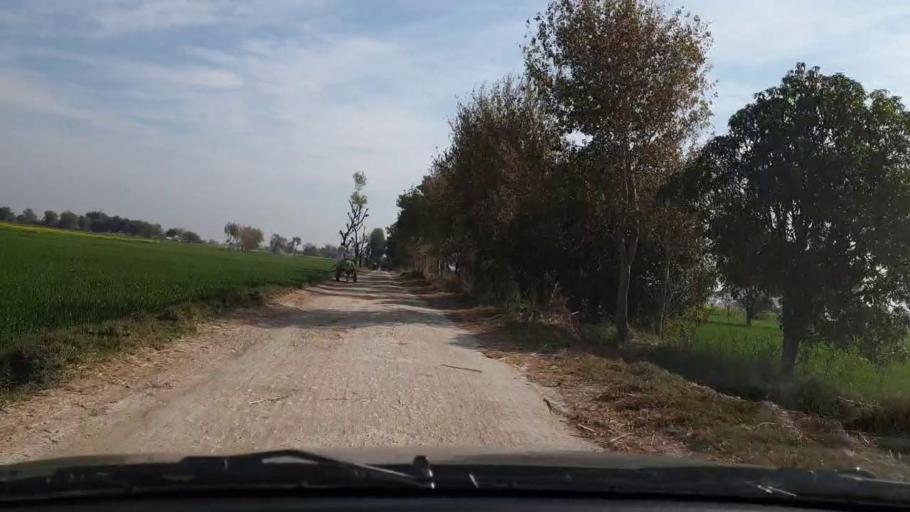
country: PK
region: Sindh
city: Jam Sahib
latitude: 26.2597
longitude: 68.6993
